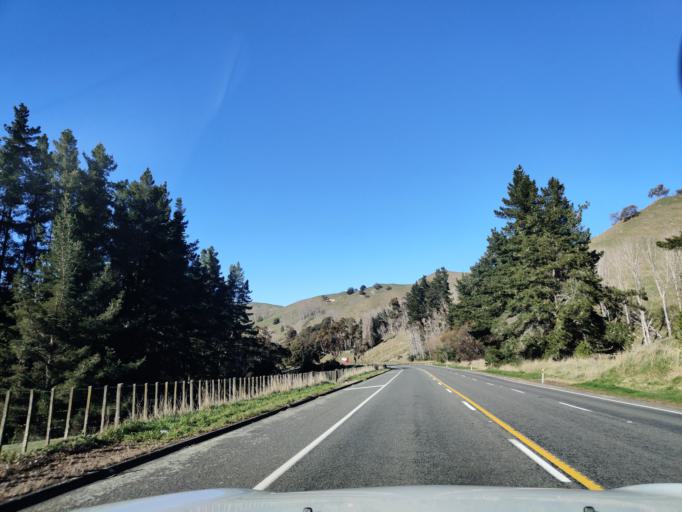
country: NZ
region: Manawatu-Wanganui
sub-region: Ruapehu District
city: Waiouru
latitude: -39.7893
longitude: 175.7852
